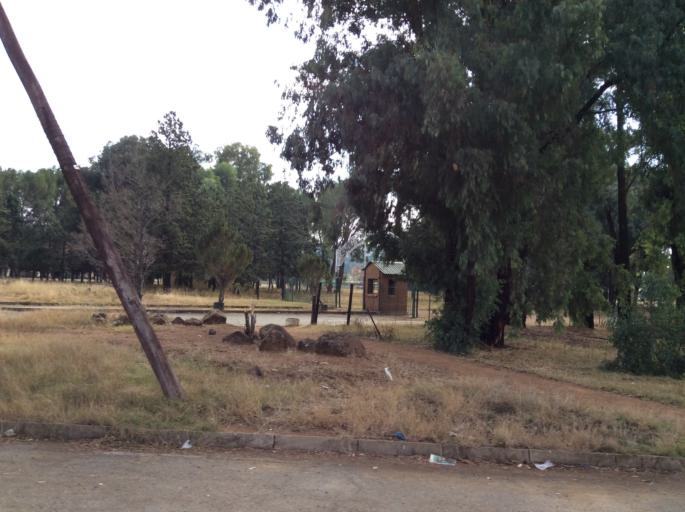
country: ZA
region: Orange Free State
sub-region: Xhariep District Municipality
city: Dewetsdorp
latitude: -29.5804
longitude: 26.6702
